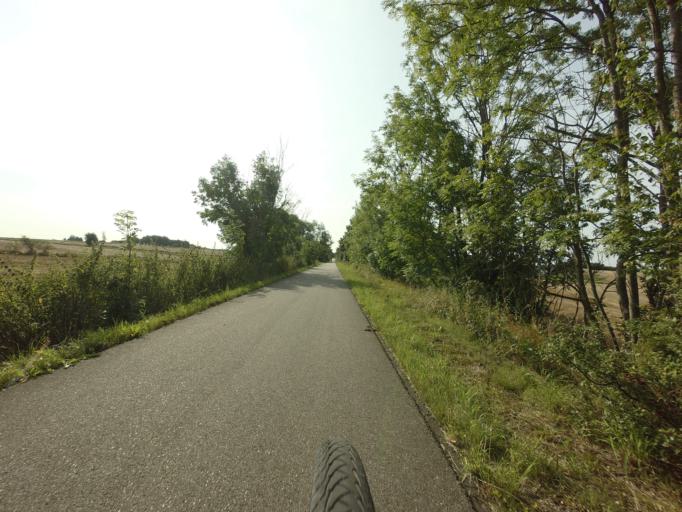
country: DK
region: Zealand
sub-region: Naestved Kommune
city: Fuglebjerg
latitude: 55.2861
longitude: 11.4286
